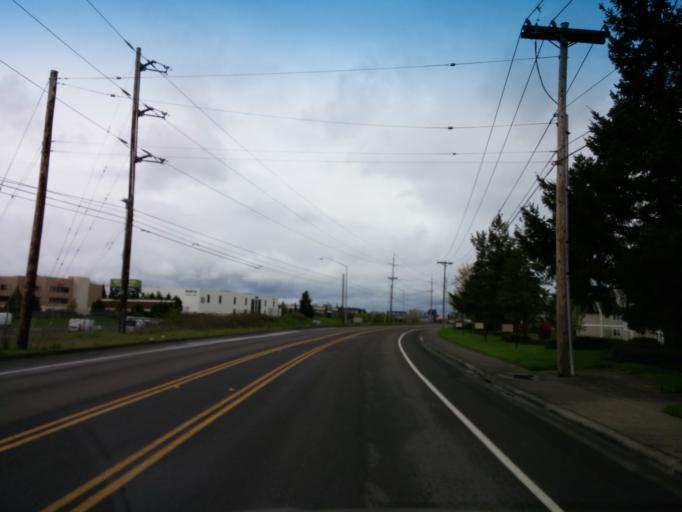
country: US
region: Oregon
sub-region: Washington County
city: Oak Hills
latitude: 45.5349
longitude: -122.8475
